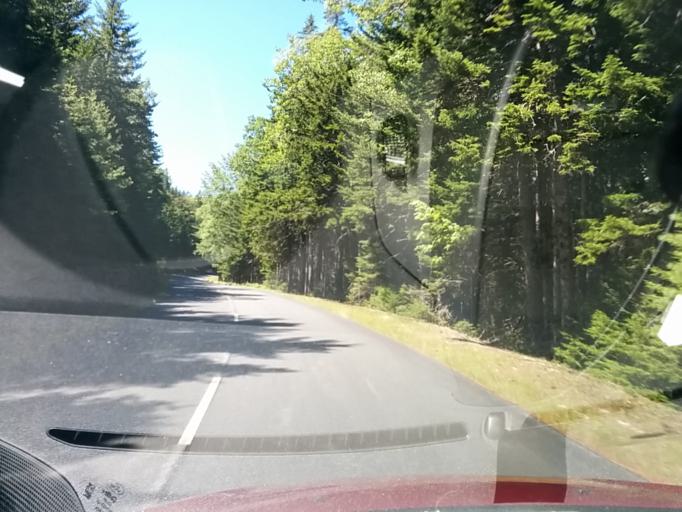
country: US
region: Maine
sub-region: Hancock County
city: Bar Harbor
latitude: 44.3174
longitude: -68.2296
